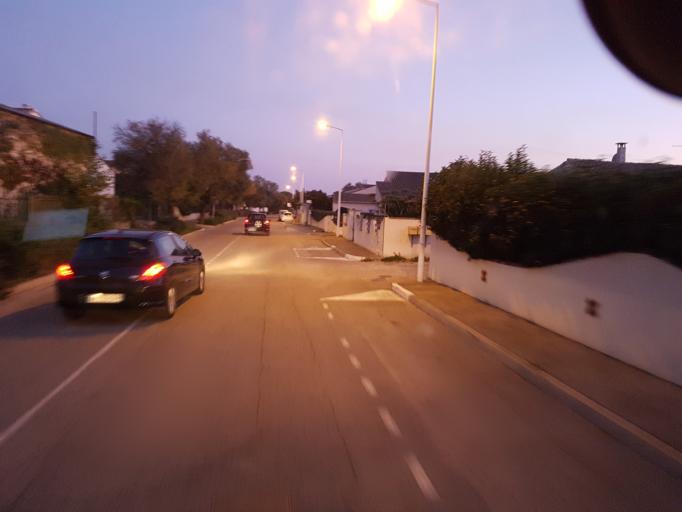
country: FR
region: Languedoc-Roussillon
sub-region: Departement du Gard
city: Bellegarde
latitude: 43.7503
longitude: 4.5182
